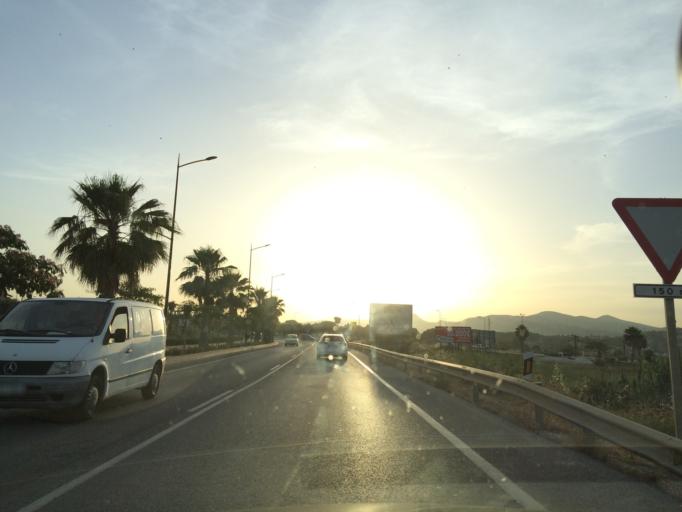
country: ES
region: Andalusia
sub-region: Provincia de Malaga
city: Alhaurin de la Torre
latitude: 36.6702
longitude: -4.5526
